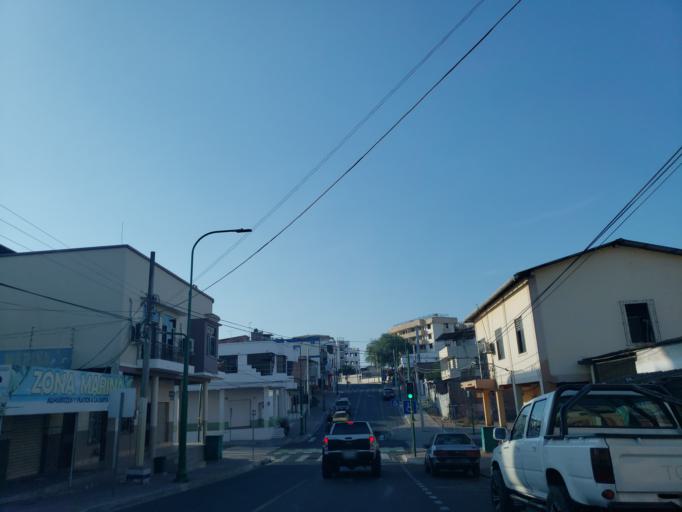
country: EC
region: Manabi
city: Manta
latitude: -0.9464
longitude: -80.7274
